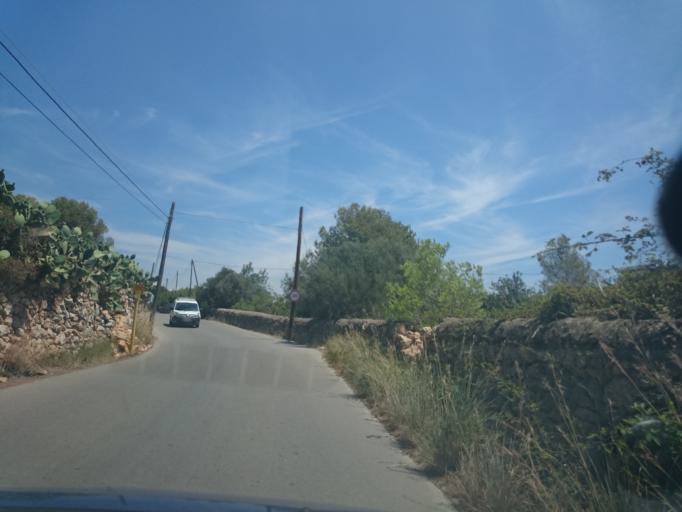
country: ES
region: Catalonia
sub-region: Provincia de Barcelona
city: Cubelles
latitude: 41.2123
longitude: 1.6906
